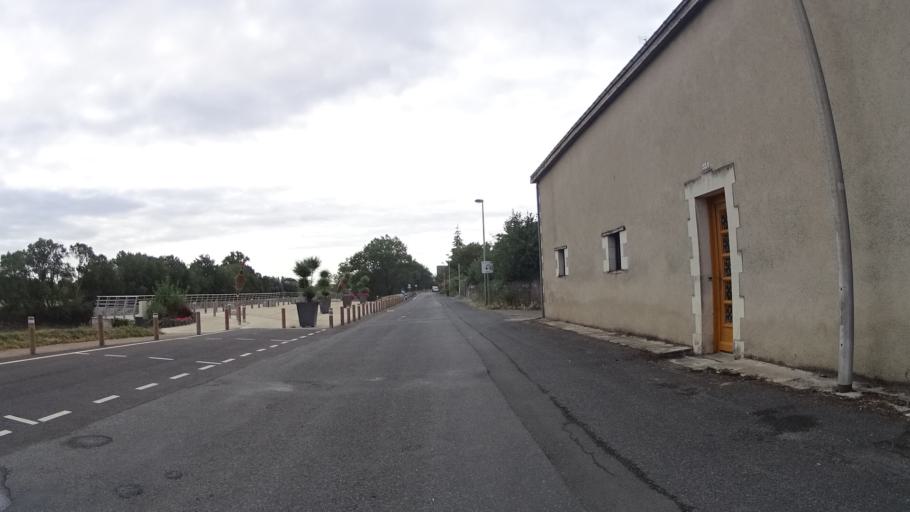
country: FR
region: Pays de la Loire
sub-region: Departement de Maine-et-Loire
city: Montjean-sur-Loire
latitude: 47.3892
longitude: -0.8565
